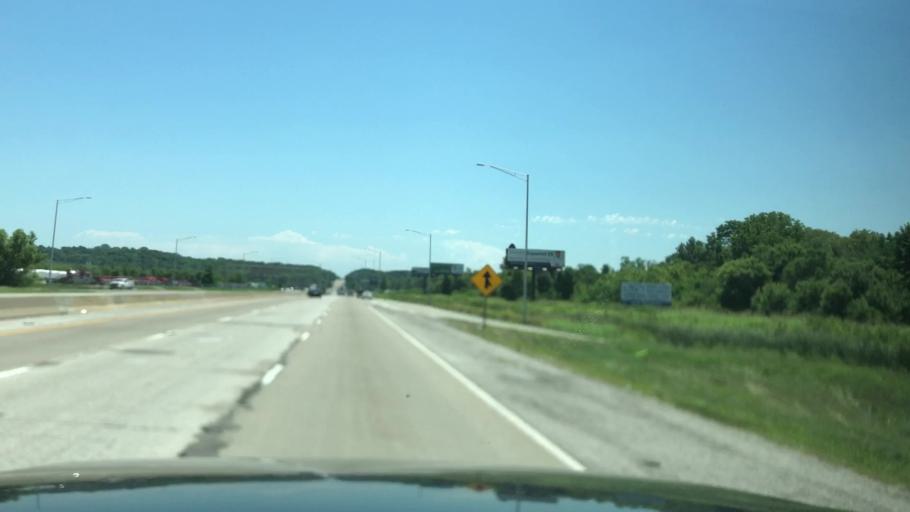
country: US
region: Illinois
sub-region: Saint Clair County
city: Alorton
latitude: 38.5806
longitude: -90.1060
